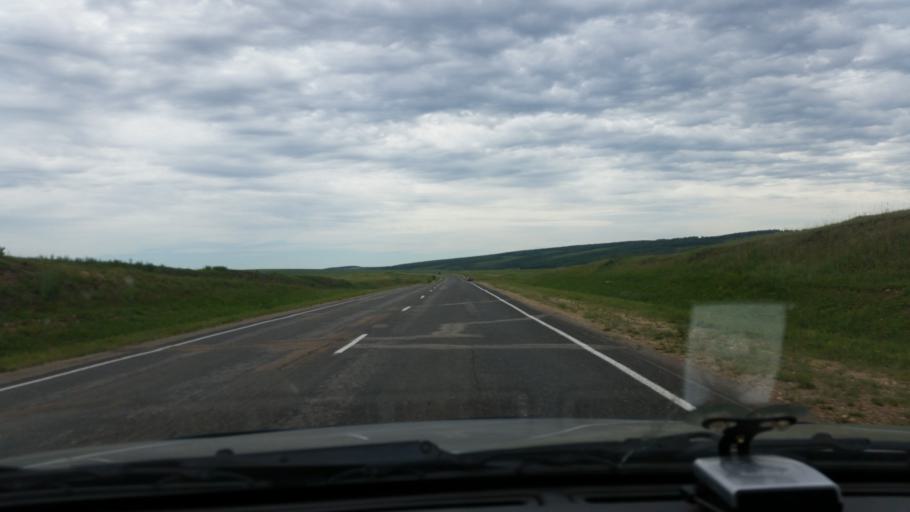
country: RU
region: Irkutsk
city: Bayanday
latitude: 52.9206
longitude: 105.1521
